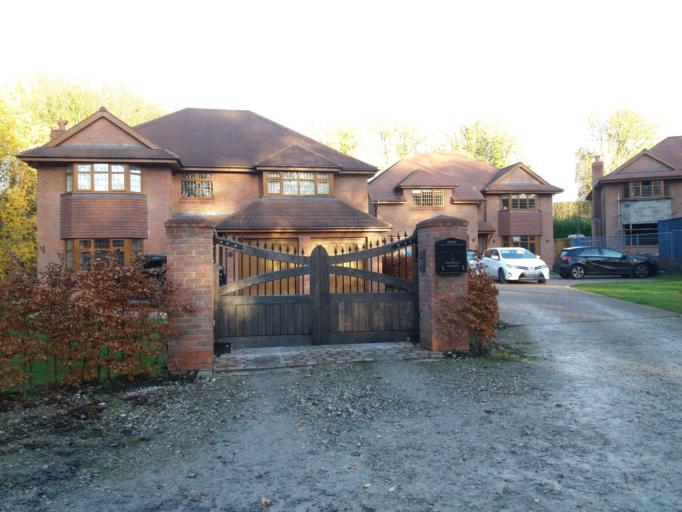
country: GB
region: England
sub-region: Lancashire
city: Euxton
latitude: 53.6643
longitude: -2.6745
